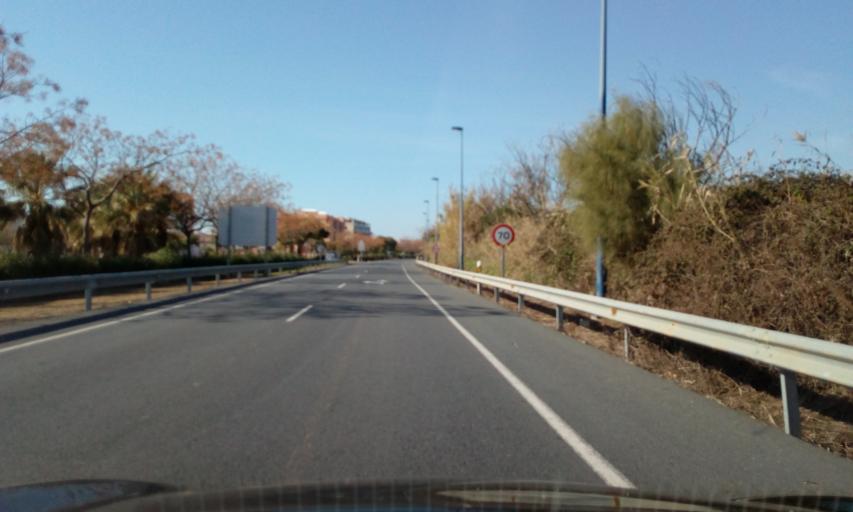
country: ES
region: Andalusia
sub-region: Provincia de Huelva
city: Lepe
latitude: 37.2108
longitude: -7.2020
